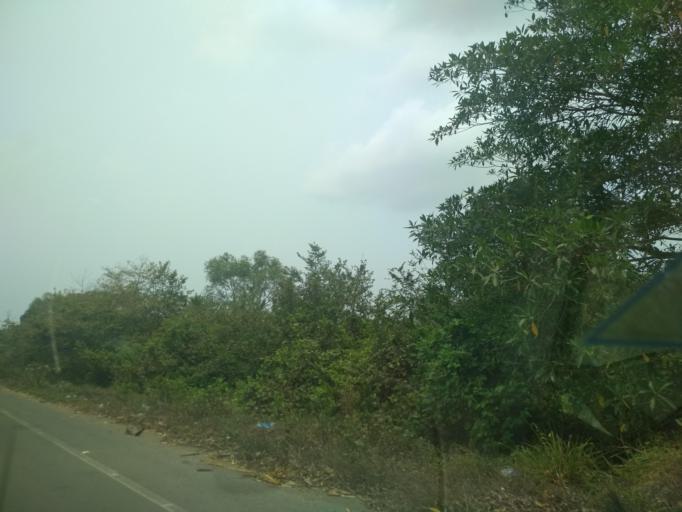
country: MX
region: Veracruz
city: Paso del Toro
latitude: 19.0285
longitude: -96.1417
